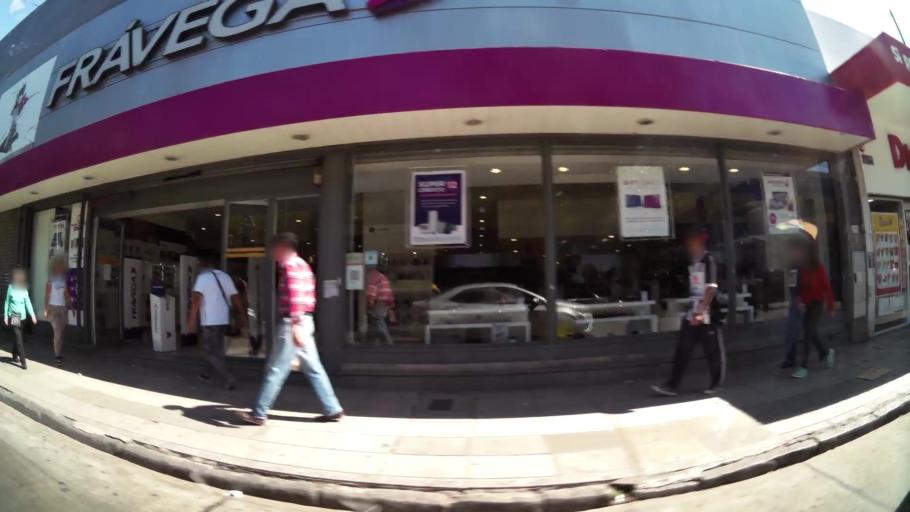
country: AR
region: Buenos Aires F.D.
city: Buenos Aires
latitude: -34.6280
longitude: -58.3836
